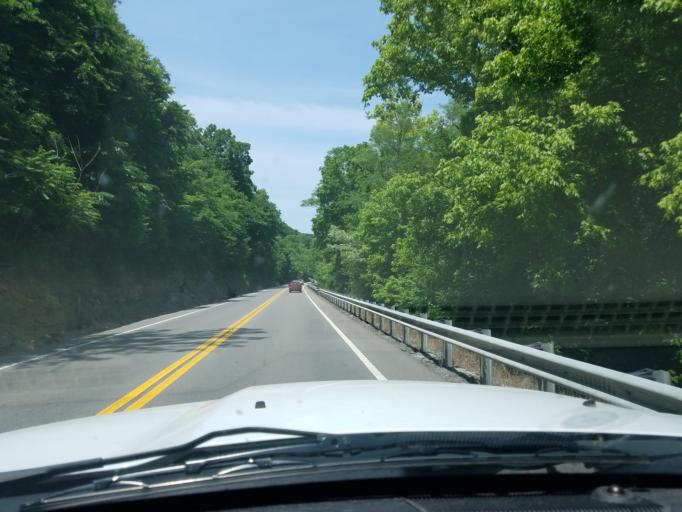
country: US
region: Tennessee
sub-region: Sumner County
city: Westmoreland
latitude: 36.4753
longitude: -86.2709
